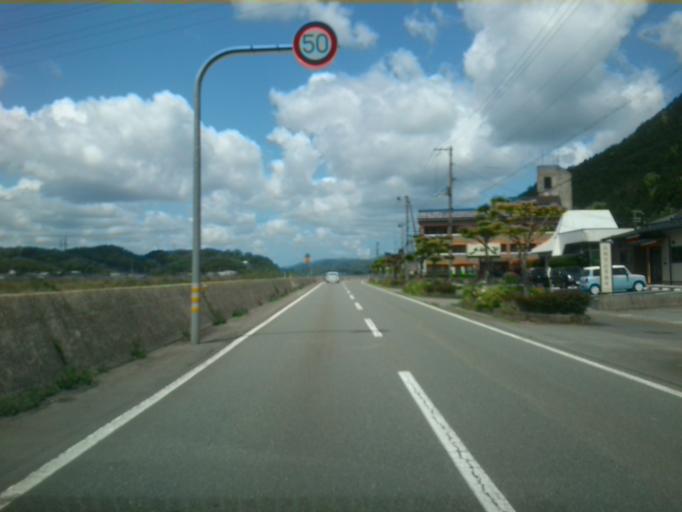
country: JP
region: Hyogo
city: Toyooka
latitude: 35.4498
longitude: 134.8724
